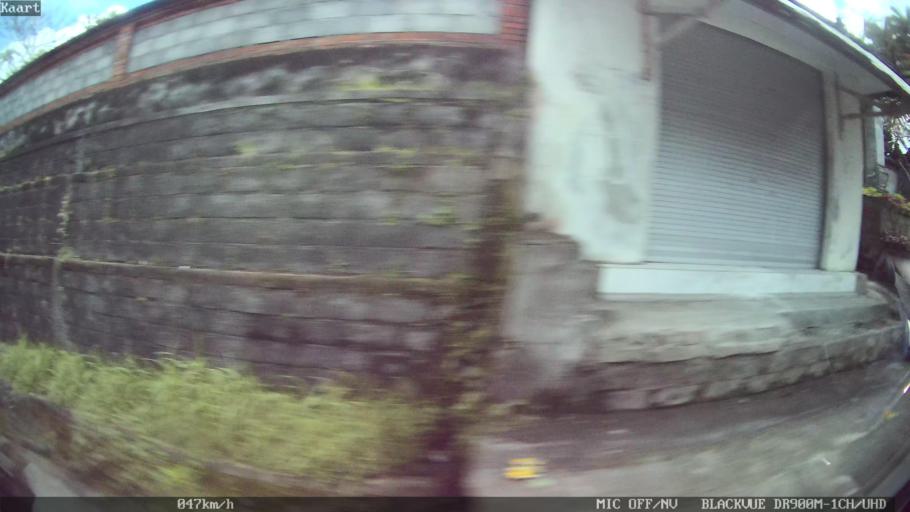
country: ID
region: Bali
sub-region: Kabupaten Gianyar
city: Ubud
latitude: -8.5379
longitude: 115.2820
